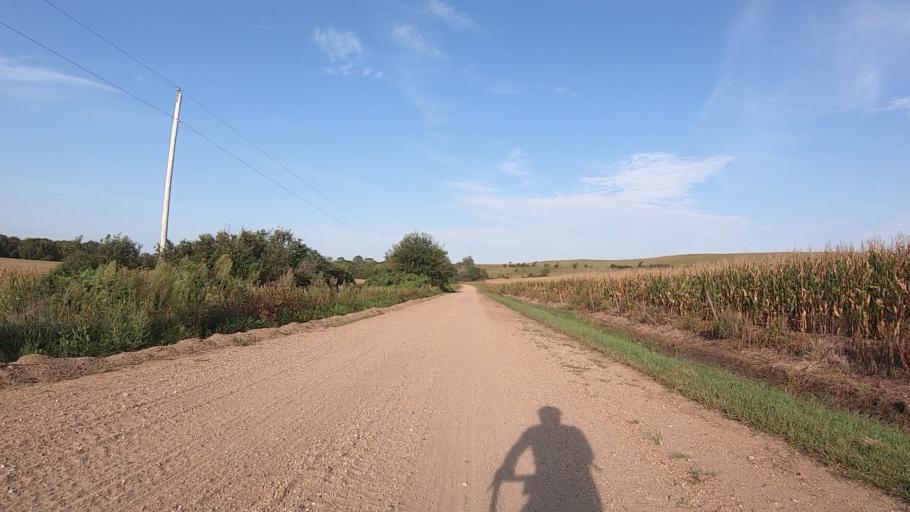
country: US
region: Kansas
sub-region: Marshall County
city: Blue Rapids
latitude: 39.6679
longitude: -96.8091
